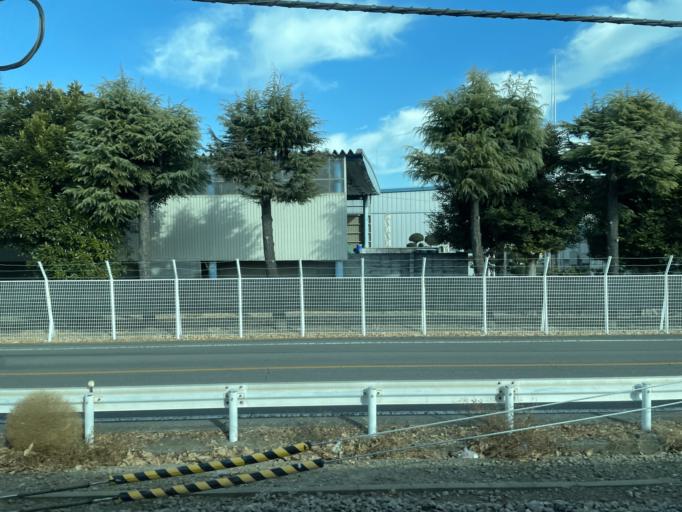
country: JP
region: Saitama
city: Fukayacho
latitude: 36.1866
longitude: 139.3011
